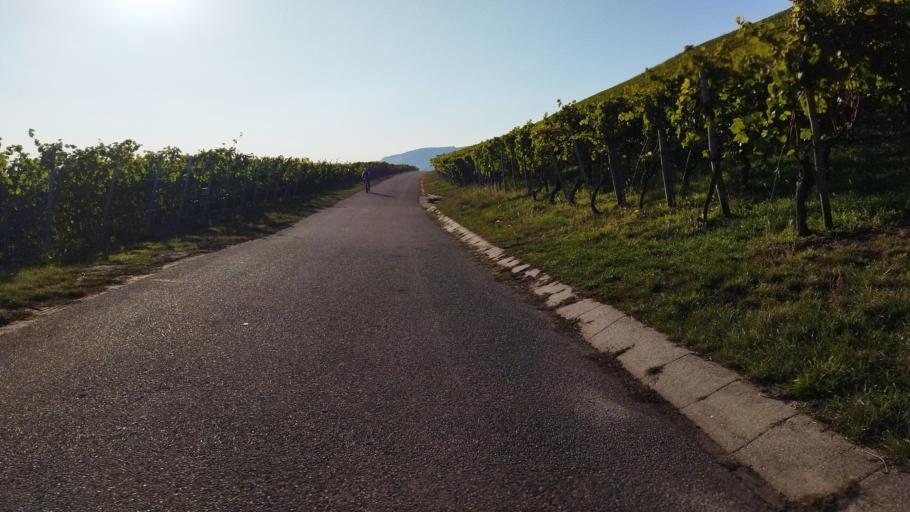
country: DE
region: Baden-Wuerttemberg
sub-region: Regierungsbezirk Stuttgart
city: Freudental
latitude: 49.0013
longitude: 9.0473
